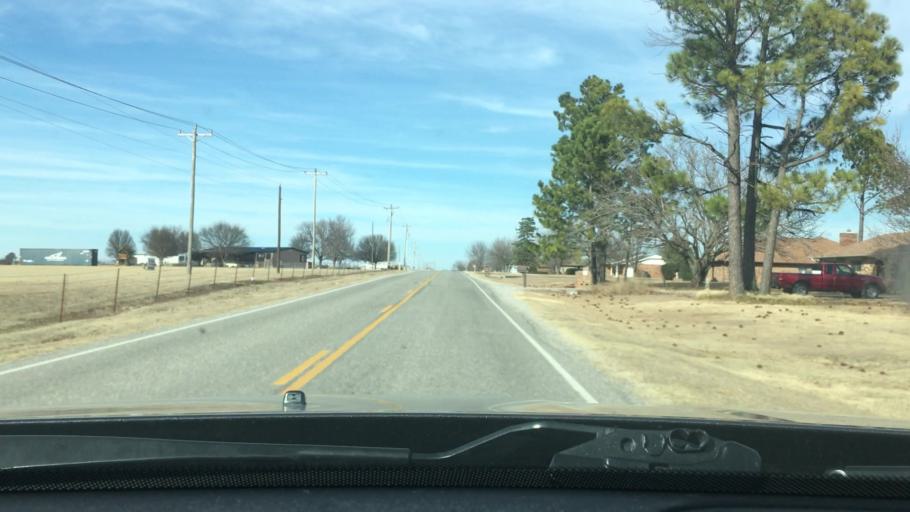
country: US
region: Oklahoma
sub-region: Murray County
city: Davis
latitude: 34.4956
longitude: -97.0904
